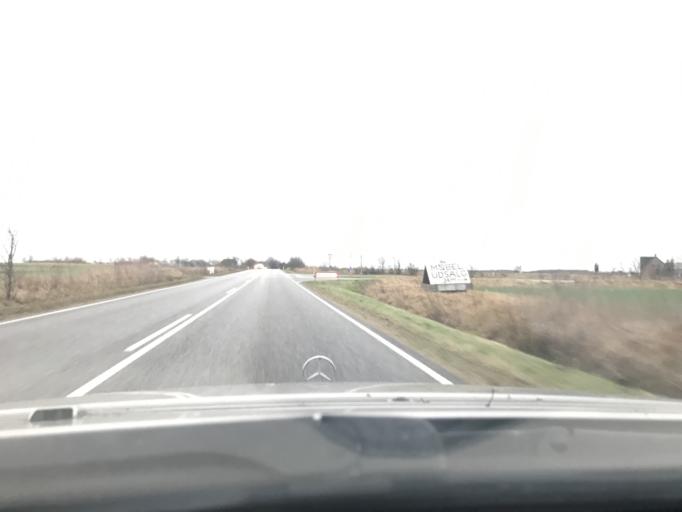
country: DK
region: South Denmark
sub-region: Aabenraa Kommune
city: Rodekro
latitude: 55.0977
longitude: 9.1916
